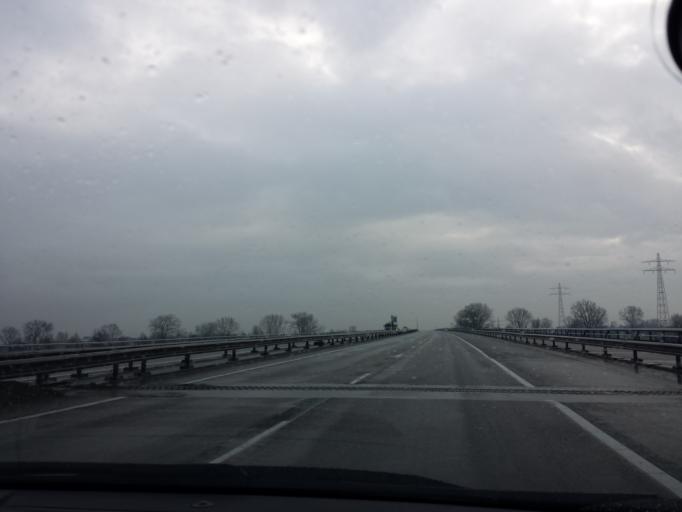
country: NL
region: North Brabant
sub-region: Gemeente Cuijk
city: Cuijk
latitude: 51.7630
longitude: 5.8372
